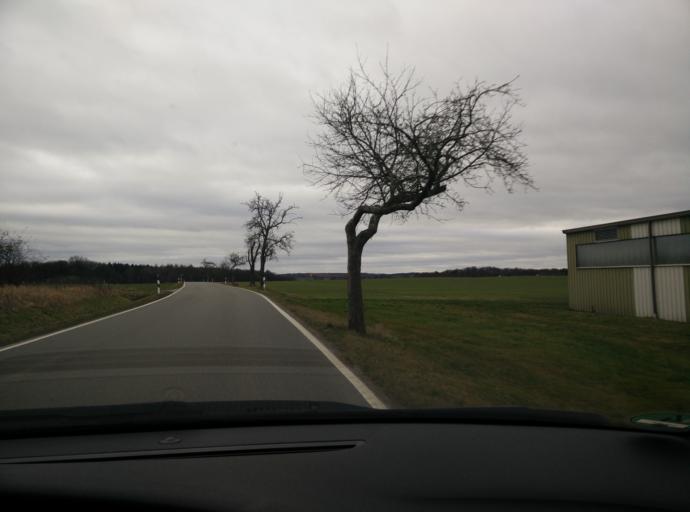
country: DE
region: Saxony
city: Geithain
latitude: 51.0268
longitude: 12.6804
